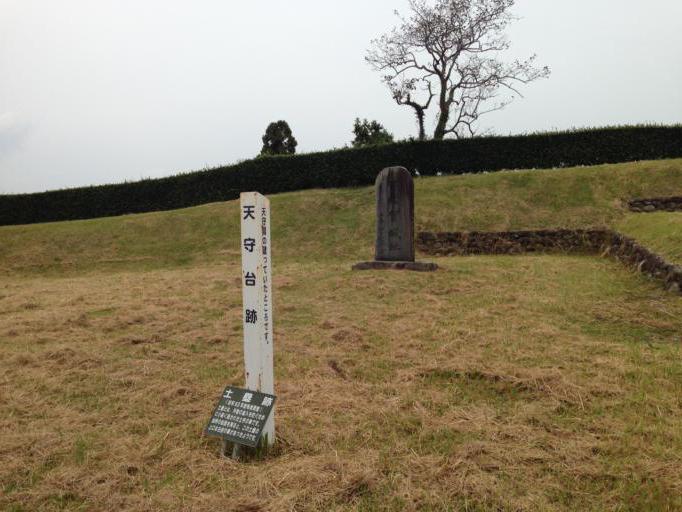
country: JP
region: Shizuoka
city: Fukuroi
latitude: 34.6855
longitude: 137.9715
